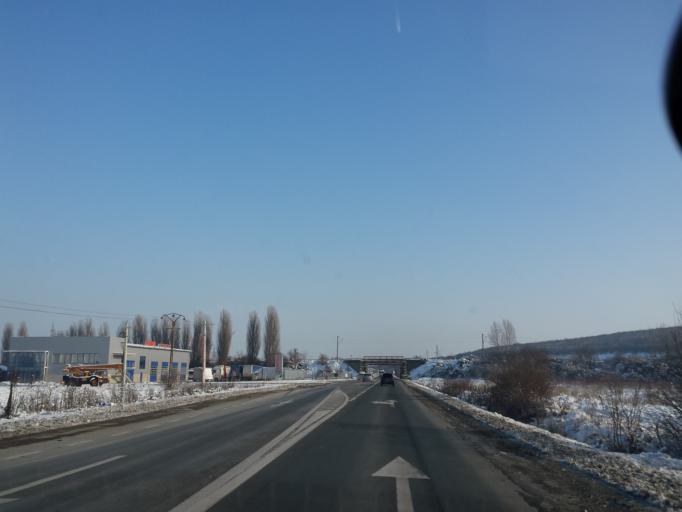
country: RO
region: Hunedoara
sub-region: Municipiul Deva
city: Cristur
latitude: 45.8511
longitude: 22.9750
